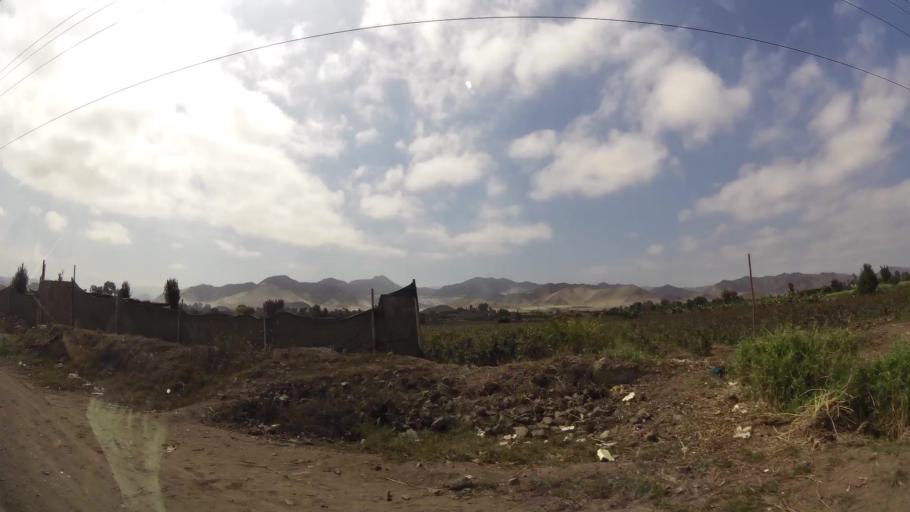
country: PE
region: Lima
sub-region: Provincia de Canete
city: Mala
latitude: -12.7007
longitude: -76.6229
